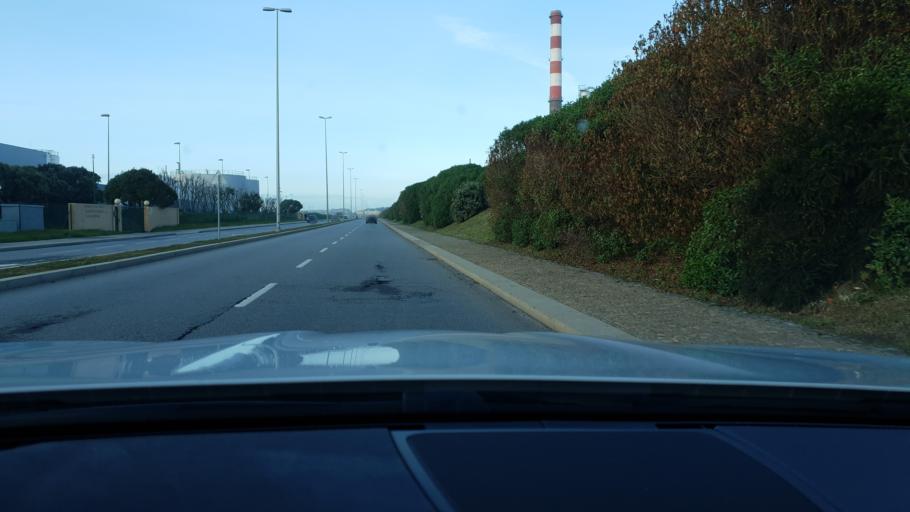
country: PT
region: Porto
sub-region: Matosinhos
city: Leca da Palmeira
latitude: 41.2104
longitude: -8.7135
